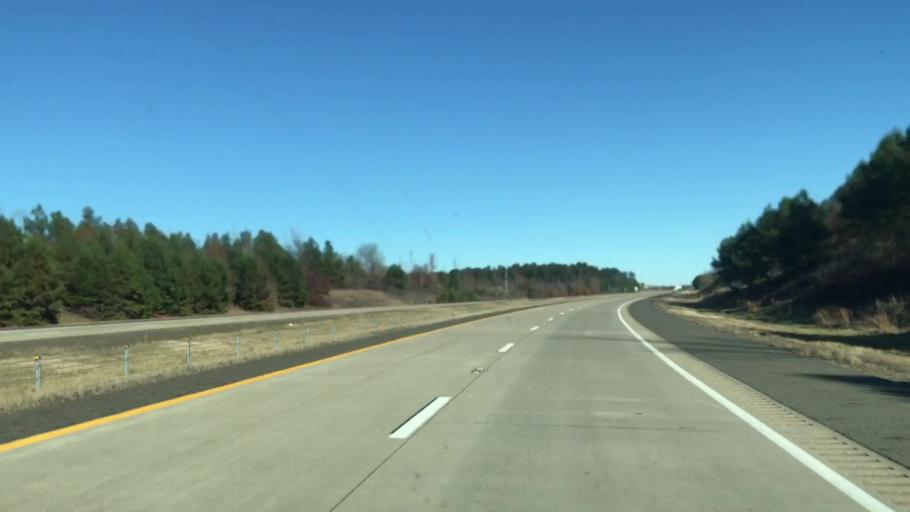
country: US
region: Louisiana
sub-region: Caddo Parish
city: Vivian
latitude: 33.1058
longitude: -93.8958
